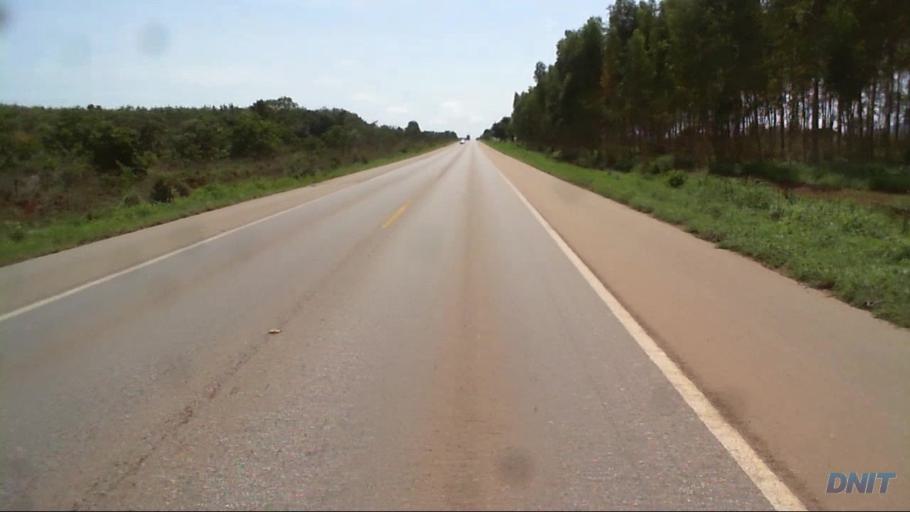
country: BR
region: Goias
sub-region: Barro Alto
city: Barro Alto
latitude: -15.2054
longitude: -48.7269
